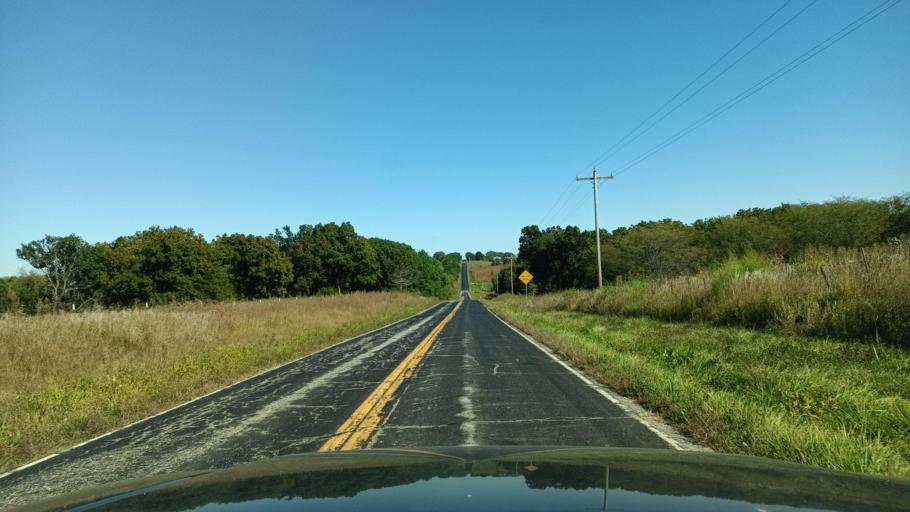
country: US
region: Missouri
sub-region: Macon County
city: La Plata
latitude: 39.9285
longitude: -92.5869
